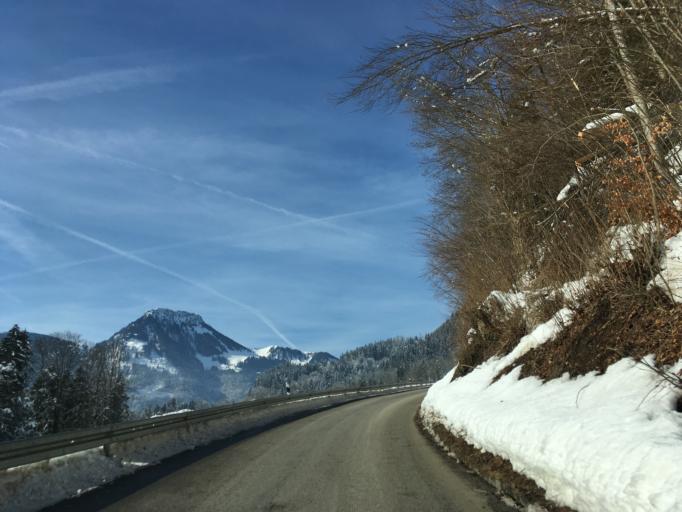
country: DE
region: Bavaria
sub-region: Upper Bavaria
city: Oberaudorf
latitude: 47.6613
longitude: 12.1472
